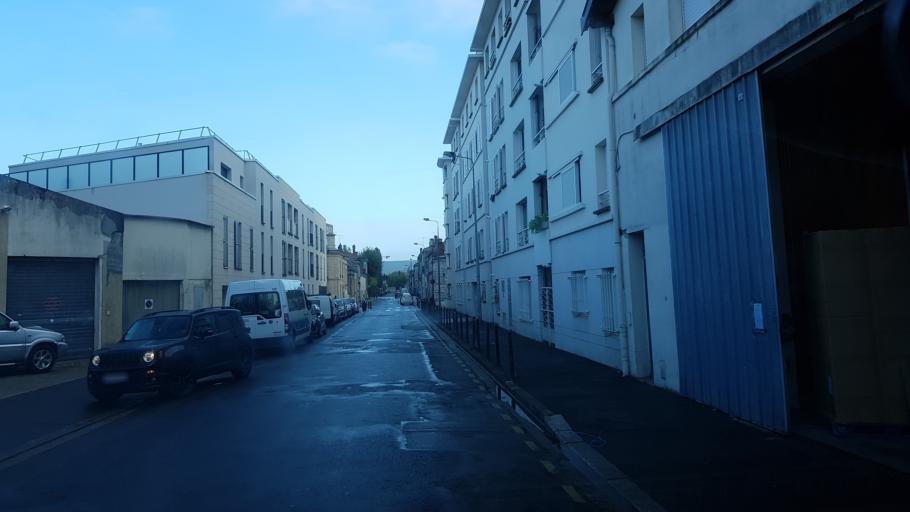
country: FR
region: Aquitaine
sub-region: Departement de la Gironde
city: Bordeaux
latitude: 44.8595
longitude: -0.5711
